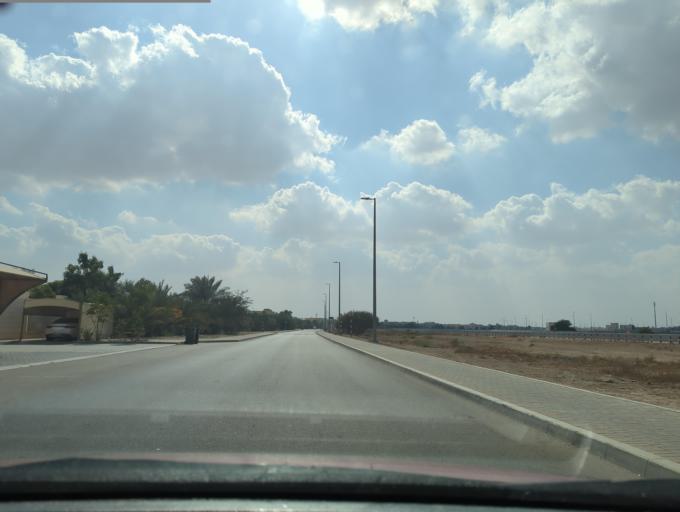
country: AE
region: Abu Dhabi
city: Al Ain
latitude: 24.1626
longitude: 55.6548
